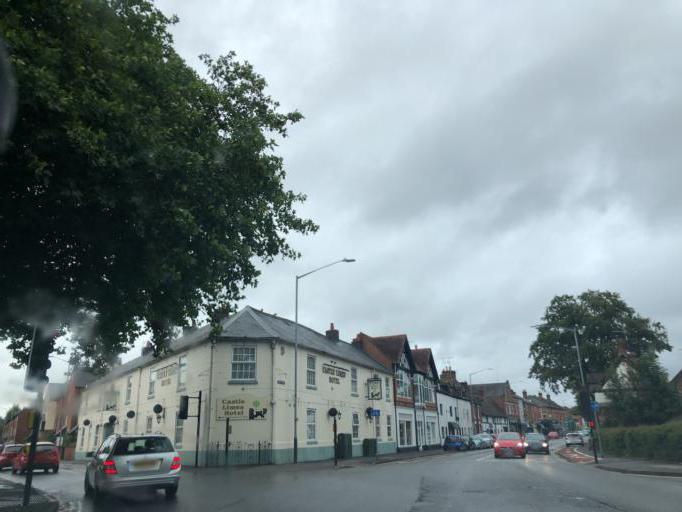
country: GB
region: England
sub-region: Warwickshire
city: Warwick
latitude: 52.2837
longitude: -1.5806
